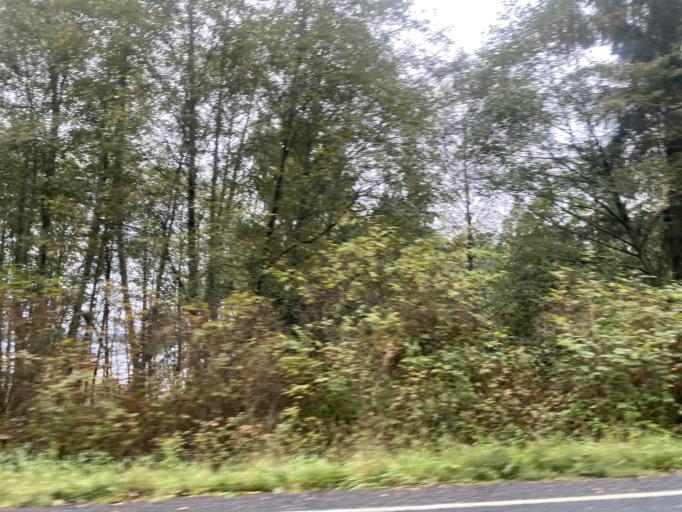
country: US
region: Washington
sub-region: Island County
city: Langley
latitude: 48.0473
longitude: -122.4380
